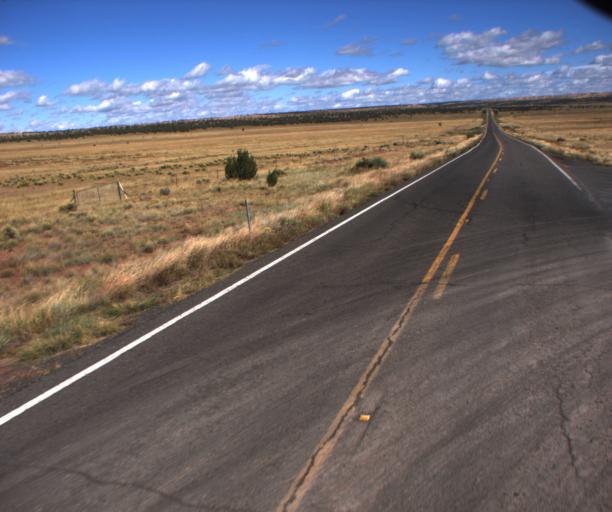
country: US
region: Arizona
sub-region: Apache County
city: Saint Johns
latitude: 34.7575
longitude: -109.2431
